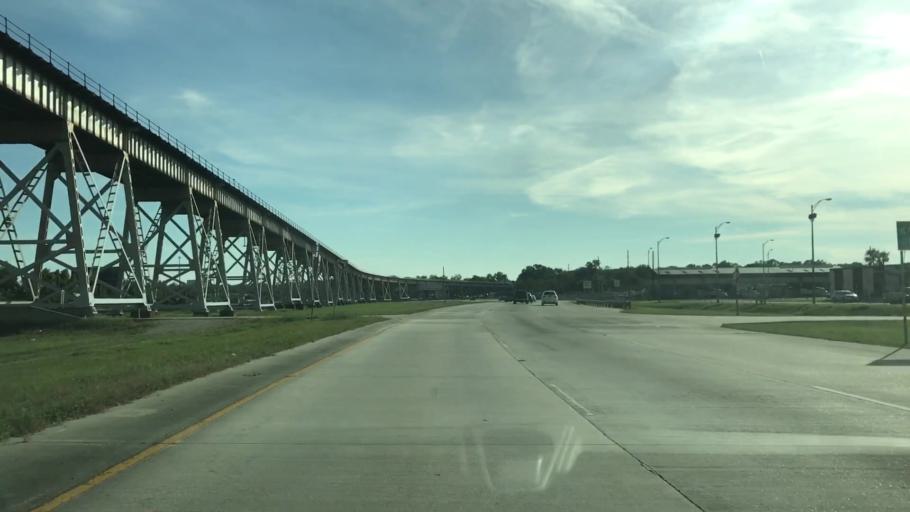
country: US
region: Louisiana
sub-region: Jefferson Parish
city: Bridge City
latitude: 29.9234
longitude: -90.1685
